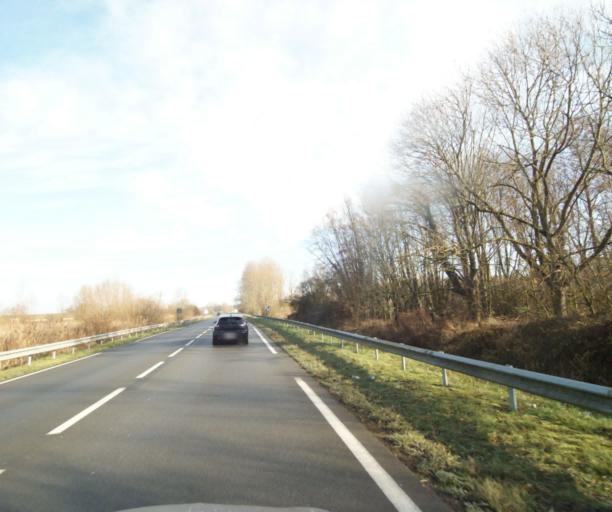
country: FR
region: Nord-Pas-de-Calais
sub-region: Departement du Nord
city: Maing
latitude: 50.3089
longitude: 3.4733
